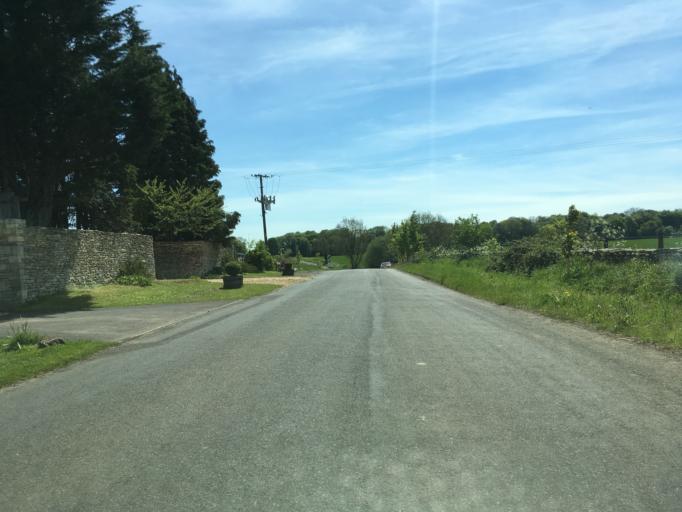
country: GB
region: England
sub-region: Gloucestershire
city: Chalford
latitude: 51.7196
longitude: -2.1174
